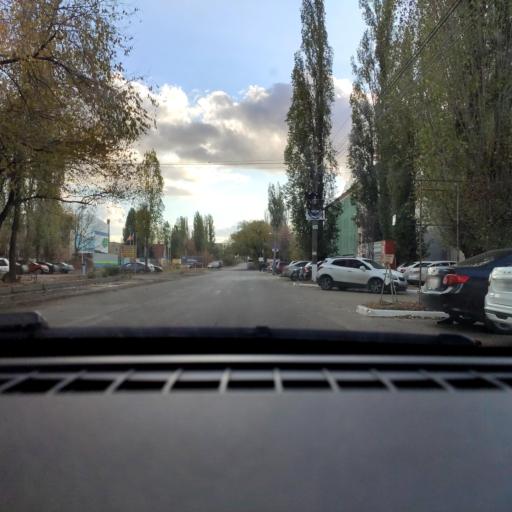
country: RU
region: Voronezj
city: Voronezh
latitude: 51.6510
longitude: 39.2891
